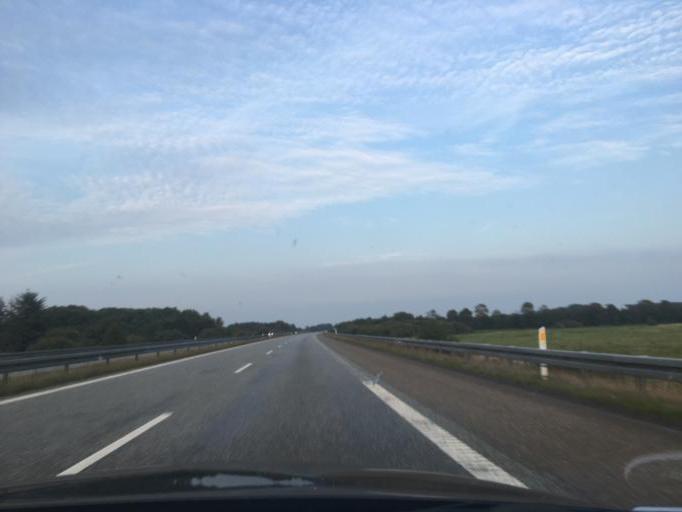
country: DK
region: South Denmark
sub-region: Esbjerg Kommune
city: Bramming
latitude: 55.5127
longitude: 8.7519
